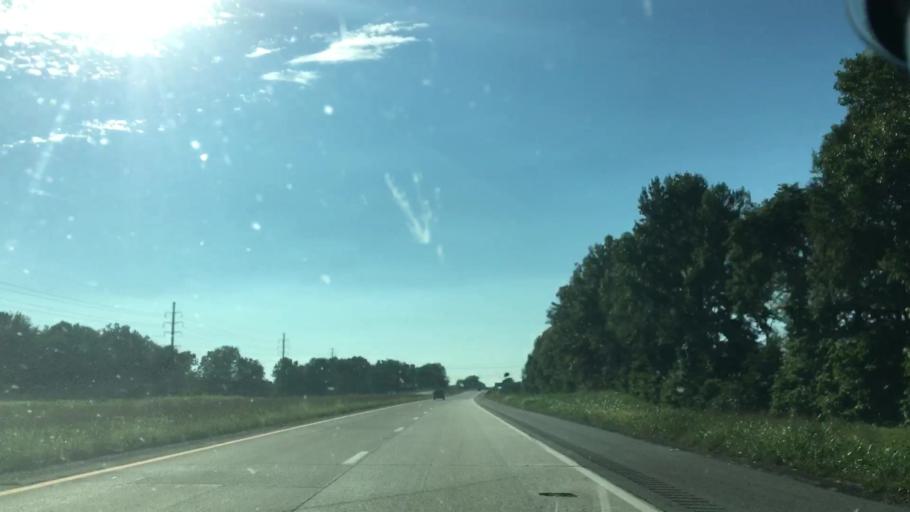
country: US
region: Kentucky
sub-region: Daviess County
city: Owensboro
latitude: 37.7657
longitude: -87.1698
